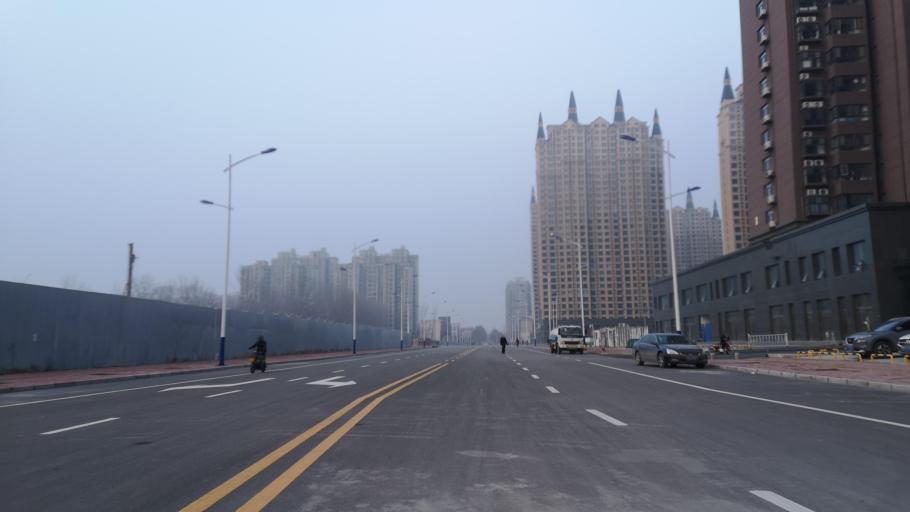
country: CN
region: Henan Sheng
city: Zhongyuanlu
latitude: 35.7482
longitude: 115.0595
